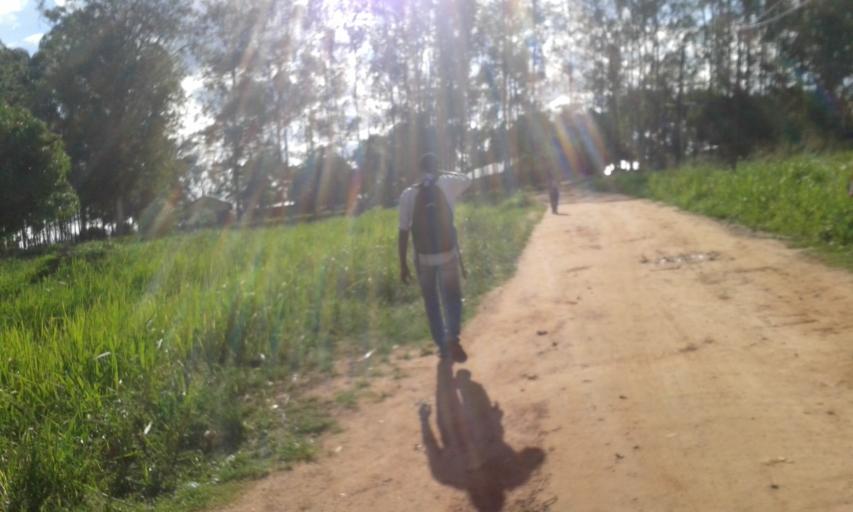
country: UG
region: Northern Region
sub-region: Gulu District
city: Gulu
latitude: 2.7973
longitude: 32.3039
